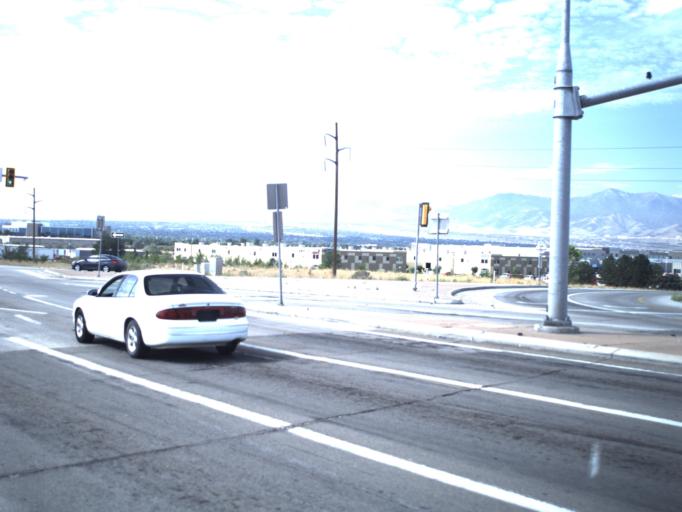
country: US
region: Utah
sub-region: Salt Lake County
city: West Valley City
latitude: 40.7253
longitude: -111.9862
